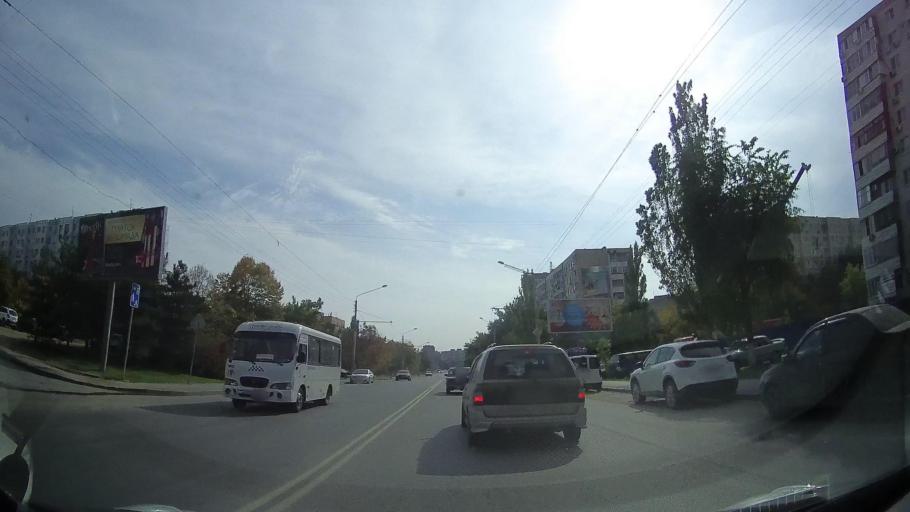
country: RU
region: Rostov
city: Severnyy
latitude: 47.2922
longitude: 39.7032
